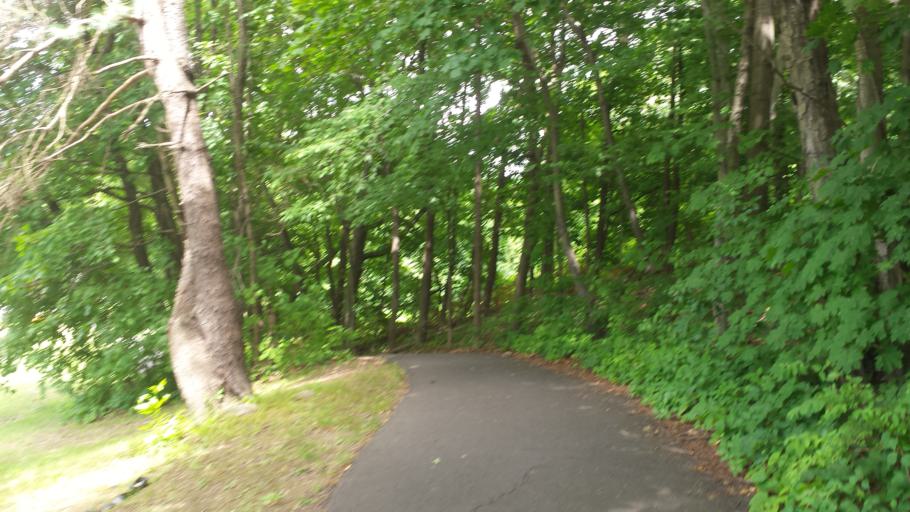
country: US
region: New York
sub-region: Westchester County
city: Valhalla
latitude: 41.0668
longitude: -73.7701
